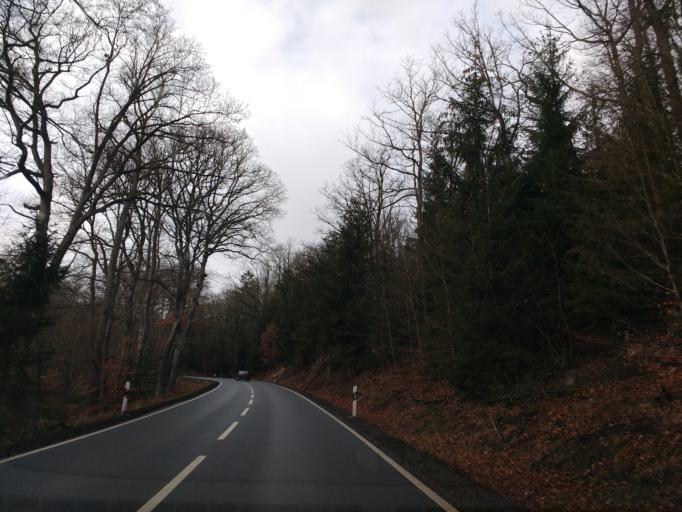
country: DE
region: Saxony-Anhalt
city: Neinstedt
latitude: 51.7130
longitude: 11.0840
